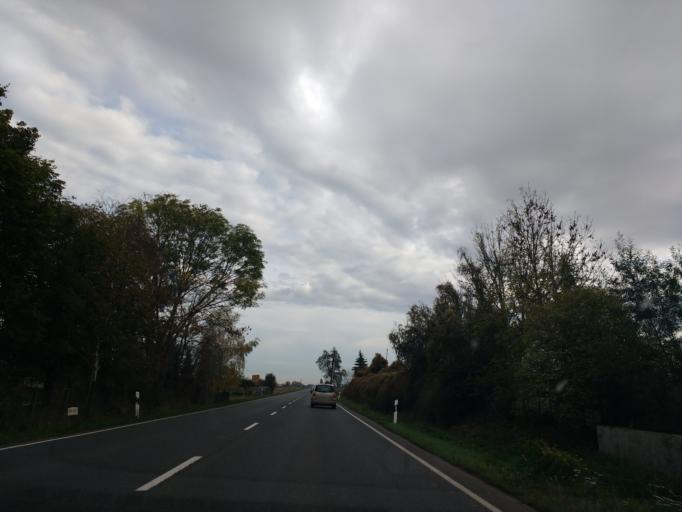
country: DE
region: Thuringia
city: Uthleben
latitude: 51.4843
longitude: 10.8460
